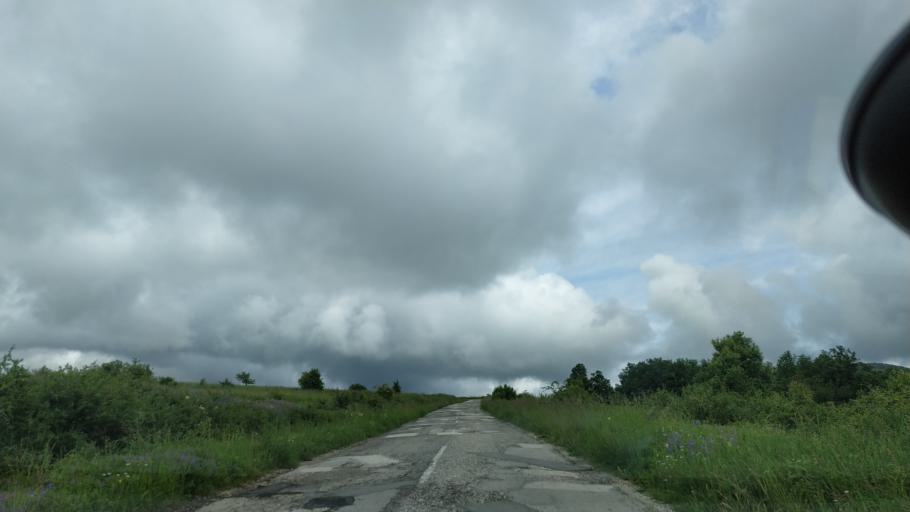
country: RS
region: Central Serbia
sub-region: Zajecarski Okrug
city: Soko Banja
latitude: 43.6965
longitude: 21.9386
